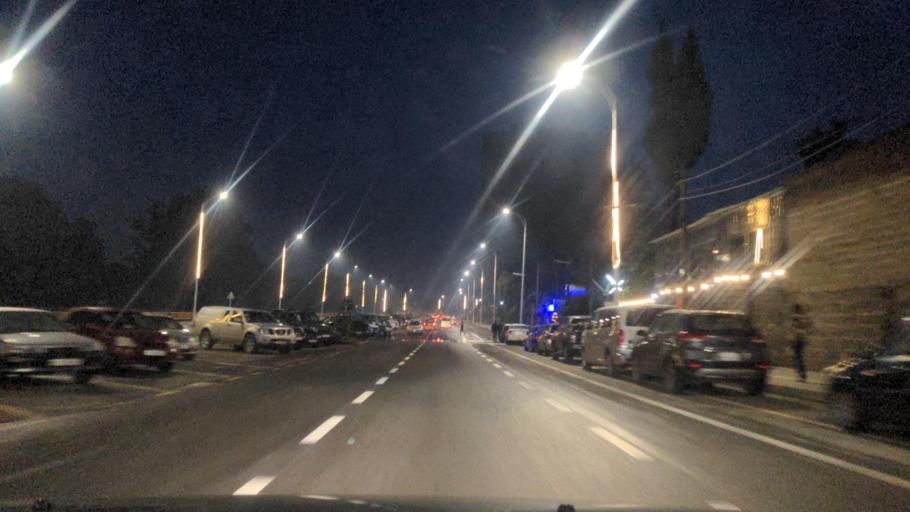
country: ET
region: Adis Abeba
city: Addis Ababa
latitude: 8.9994
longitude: 38.7738
